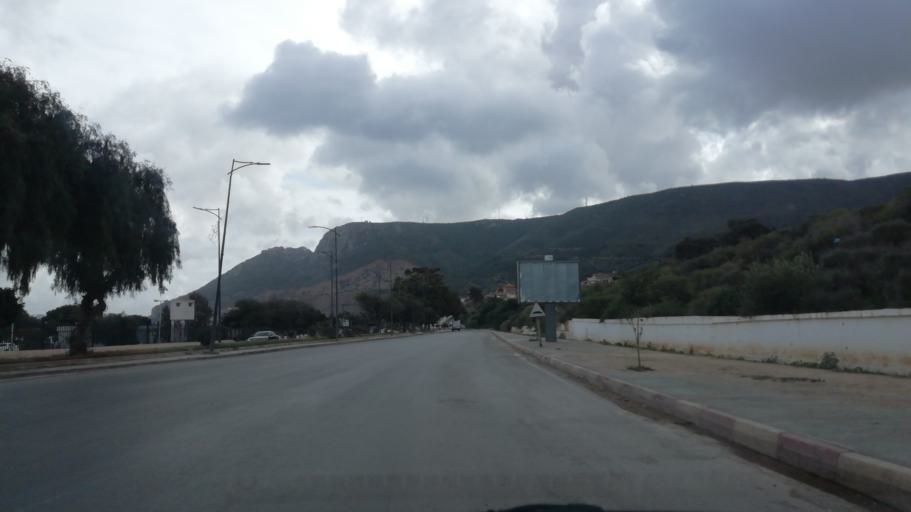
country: DZ
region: Oran
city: Mers el Kebir
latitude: 35.7181
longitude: -0.6983
